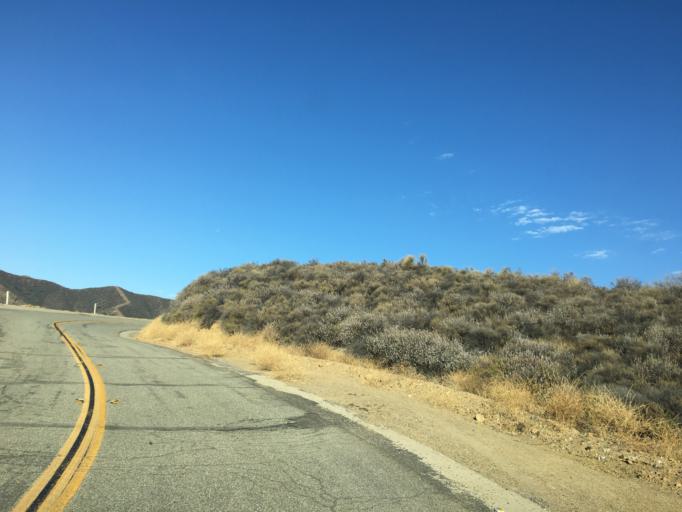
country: US
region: California
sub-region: Los Angeles County
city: Castaic
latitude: 34.5485
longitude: -118.6556
